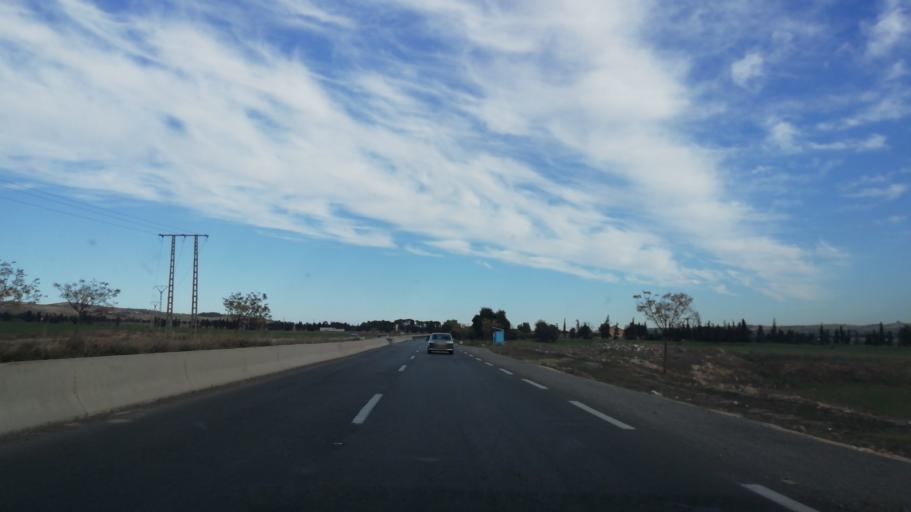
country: DZ
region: Sidi Bel Abbes
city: Sfizef
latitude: 35.1857
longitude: -0.3866
